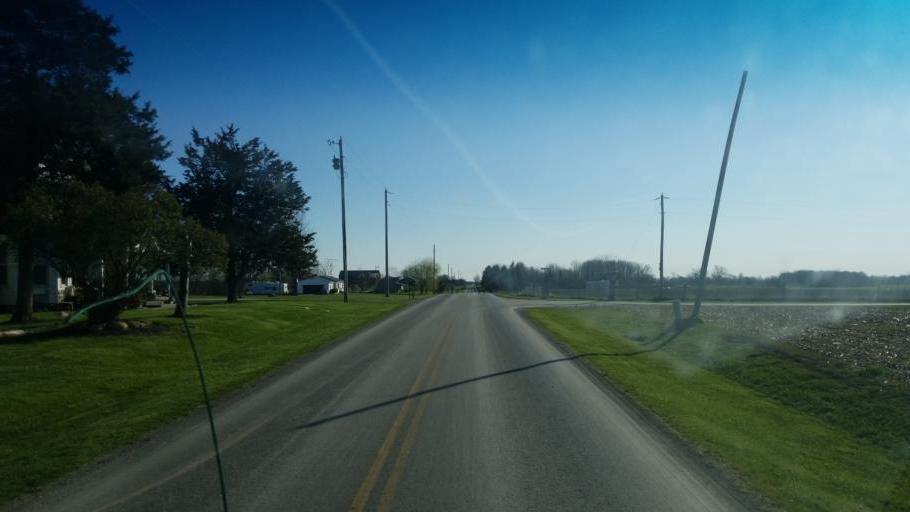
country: US
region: Ohio
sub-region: Hardin County
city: Kenton
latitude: 40.5440
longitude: -83.6026
